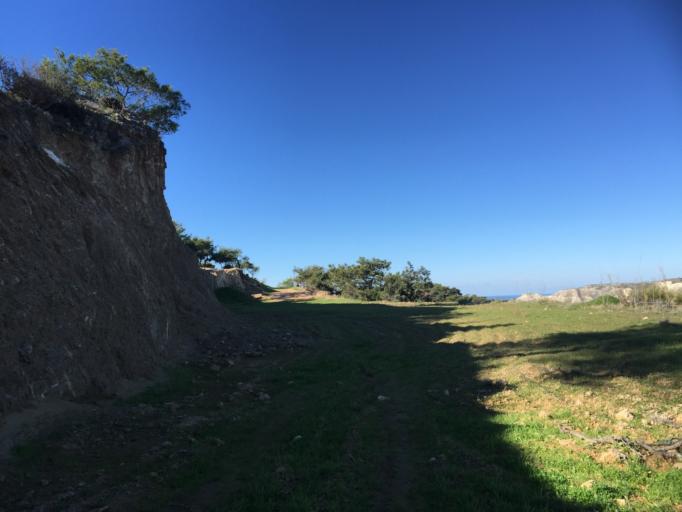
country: CY
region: Limassol
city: Pissouri
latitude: 34.6688
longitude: 32.6846
